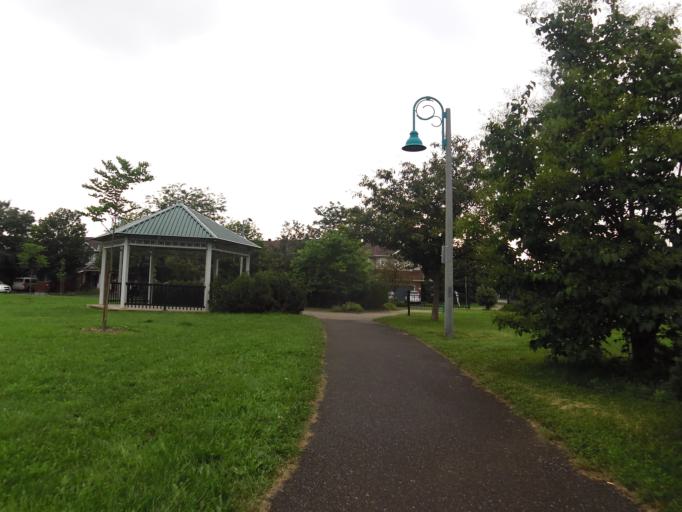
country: CA
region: Ontario
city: Bells Corners
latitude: 45.3181
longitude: -75.8946
